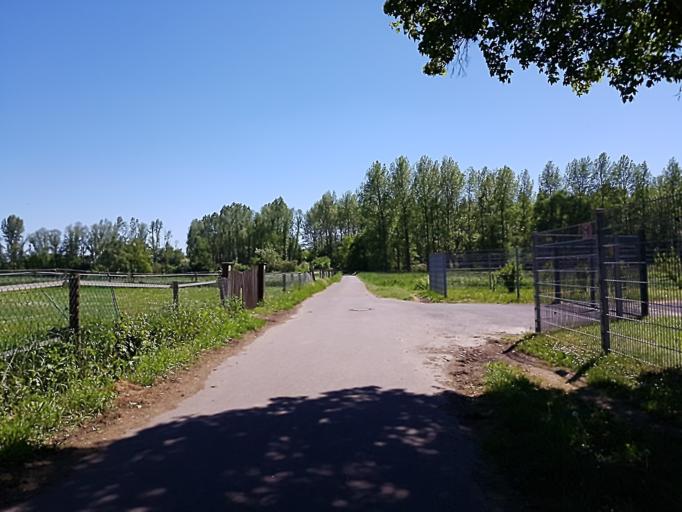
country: DE
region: North Rhine-Westphalia
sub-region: Regierungsbezirk Dusseldorf
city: Grefrath
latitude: 51.3292
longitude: 6.3732
